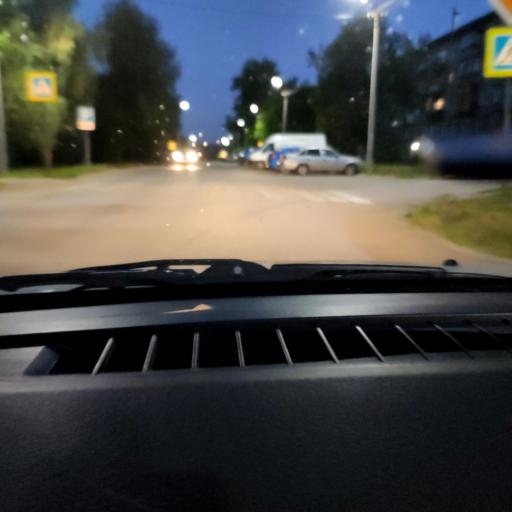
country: RU
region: Perm
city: Zvezdnyy
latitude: 57.7367
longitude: 56.3219
